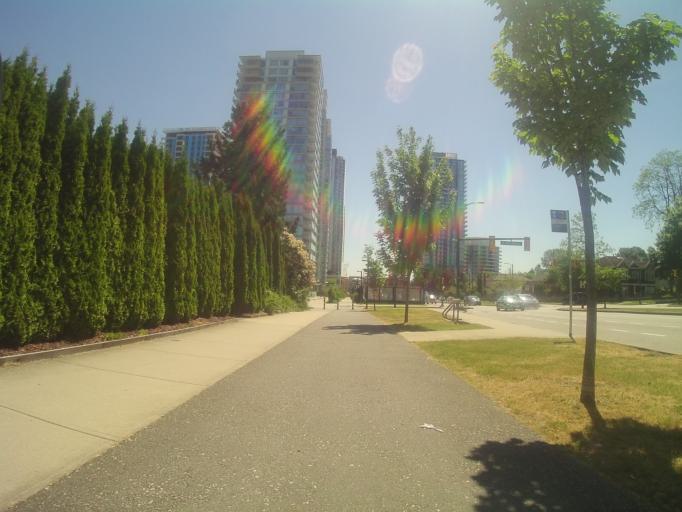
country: CA
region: British Columbia
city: Vancouver
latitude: 49.2127
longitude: -123.1168
